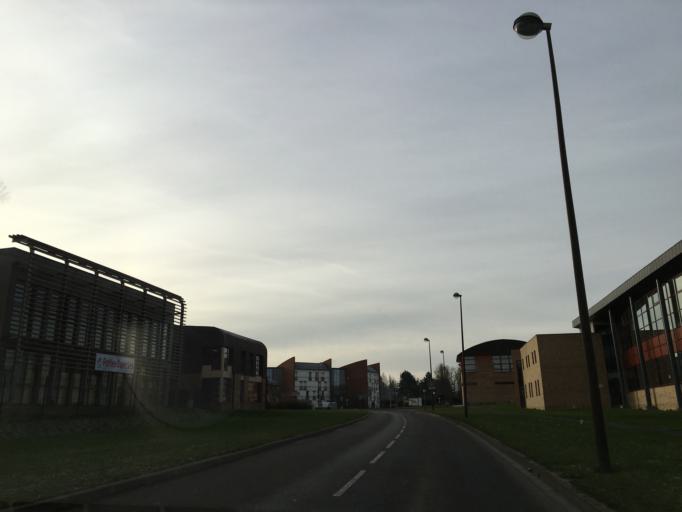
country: FR
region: Nord-Pas-de-Calais
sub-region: Departement du Pas-de-Calais
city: Saint-Laurent-Blangy
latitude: 50.2838
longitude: 2.7955
